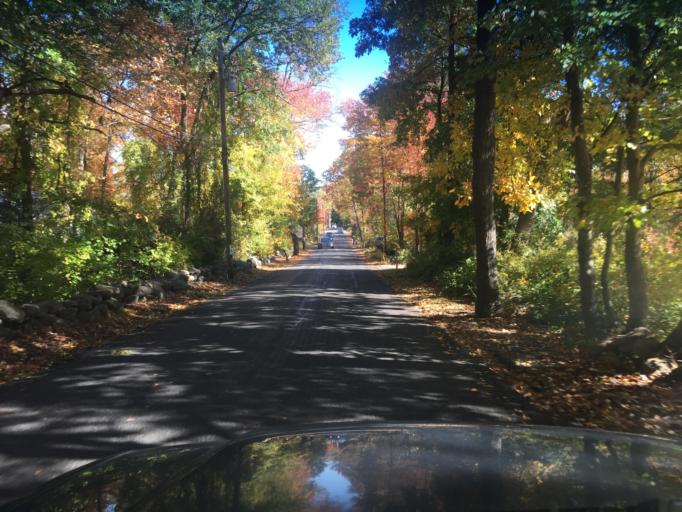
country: US
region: Massachusetts
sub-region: Middlesex County
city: Stow
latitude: 42.4125
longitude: -71.5179
